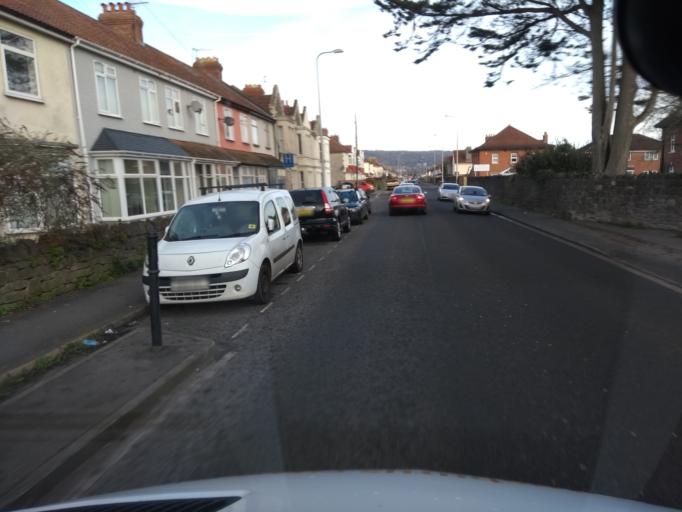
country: GB
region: England
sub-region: North Somerset
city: Weston-super-Mare
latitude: 51.3389
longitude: -2.9696
